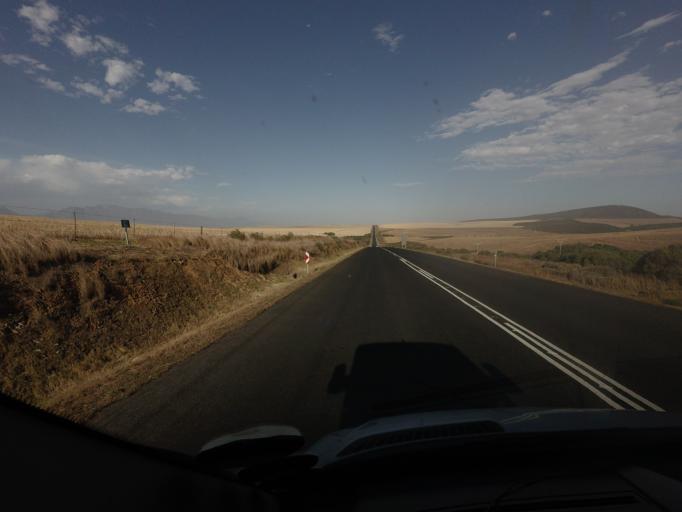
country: ZA
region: Western Cape
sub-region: Overberg District Municipality
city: Swellendam
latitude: -34.1059
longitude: 20.2713
